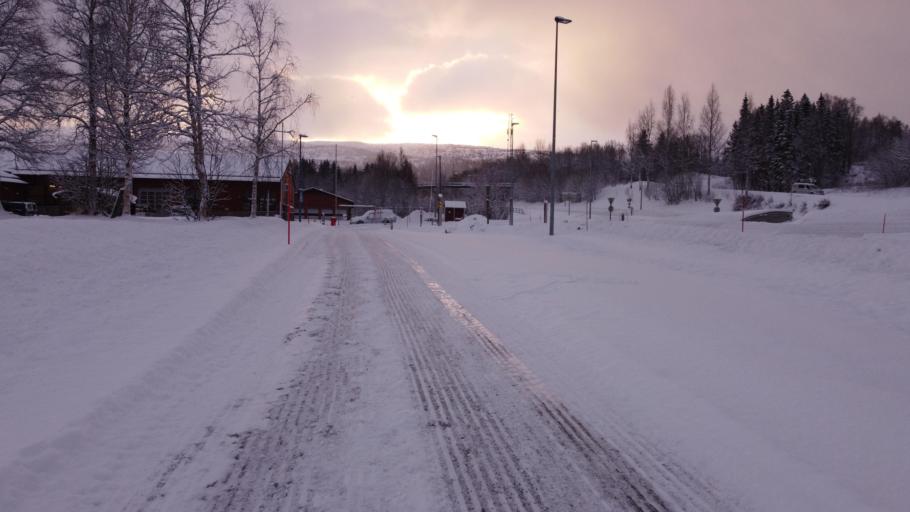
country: NO
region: Nordland
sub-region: Rana
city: Mo i Rana
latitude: 66.3285
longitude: 14.1598
